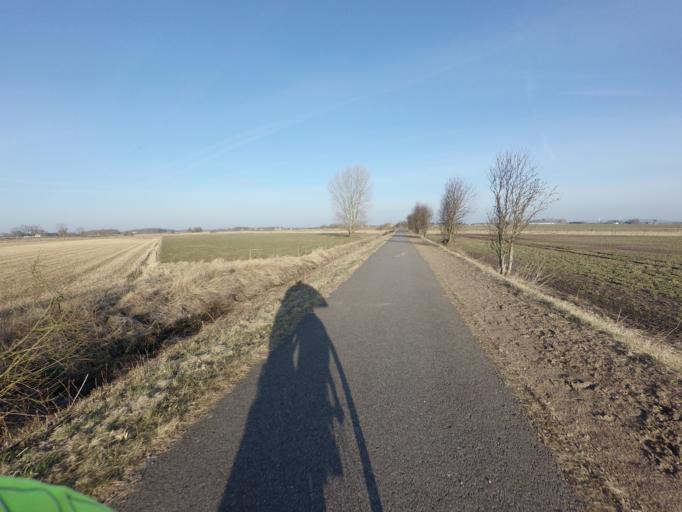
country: SE
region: Skane
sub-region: Hoganas Kommun
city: Hoganas
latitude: 56.1894
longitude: 12.6226
